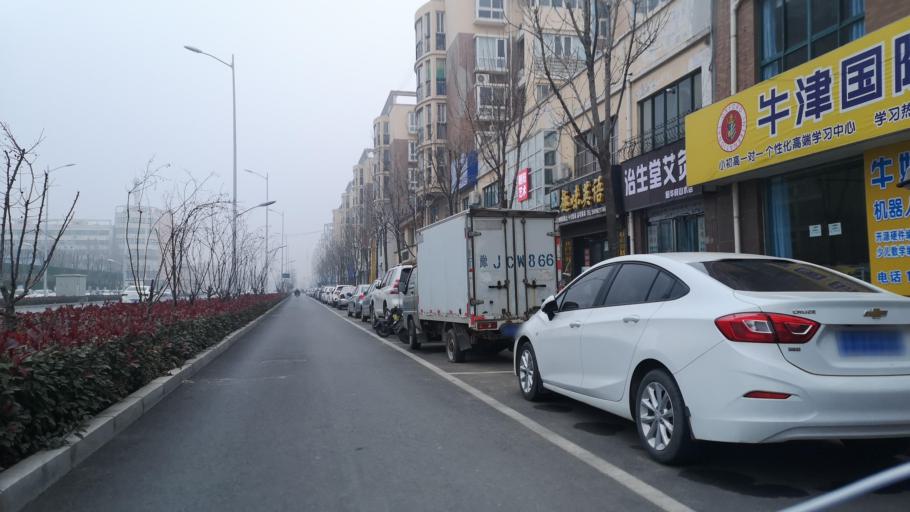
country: CN
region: Henan Sheng
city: Zhongyuanlu
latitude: 35.7648
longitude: 115.0847
